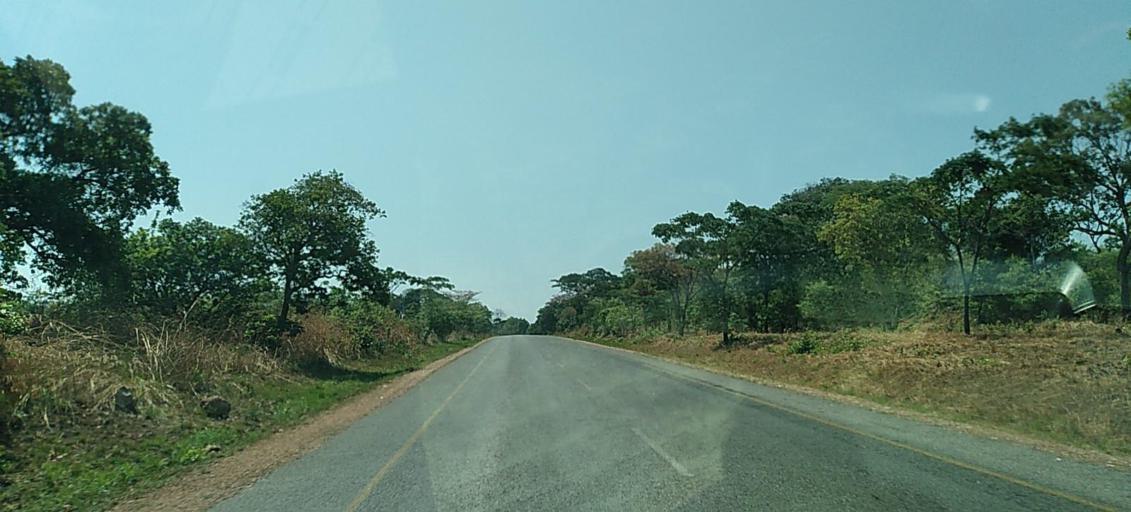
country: ZM
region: North-Western
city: Solwezi
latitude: -12.2891
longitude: 25.7919
